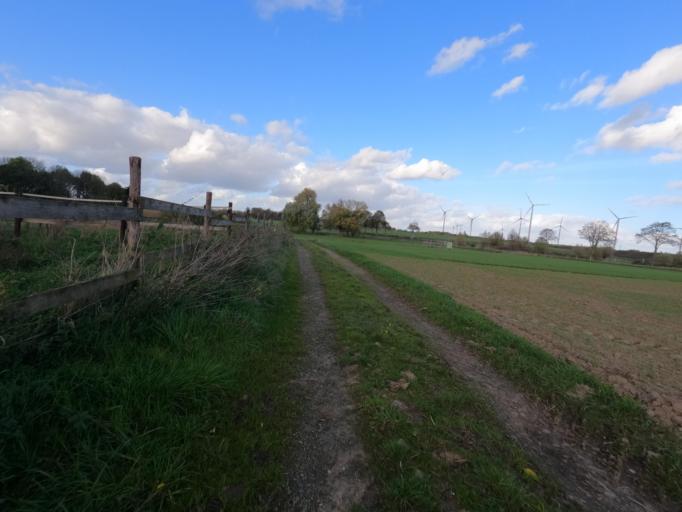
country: DE
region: North Rhine-Westphalia
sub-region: Regierungsbezirk Koln
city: Titz
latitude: 51.0847
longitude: 6.4177
